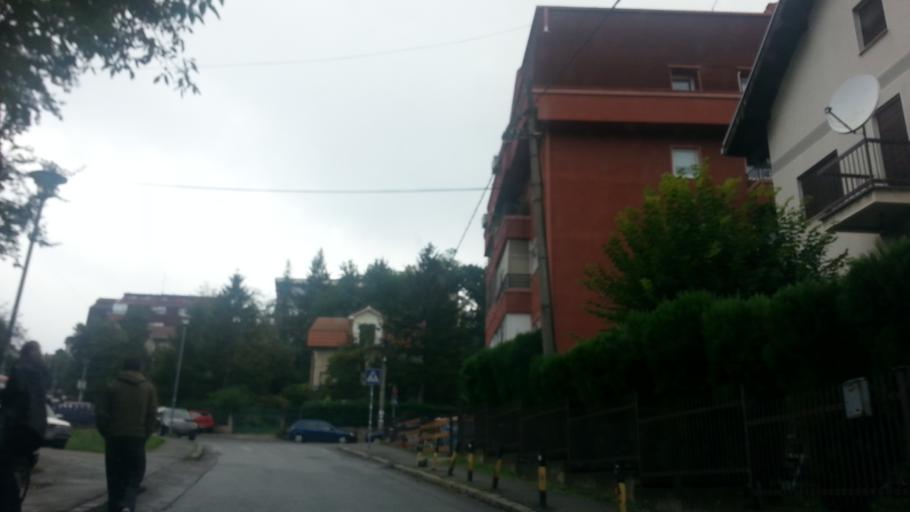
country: RS
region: Central Serbia
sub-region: Belgrade
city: Rakovica
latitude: 44.7458
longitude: 20.4370
